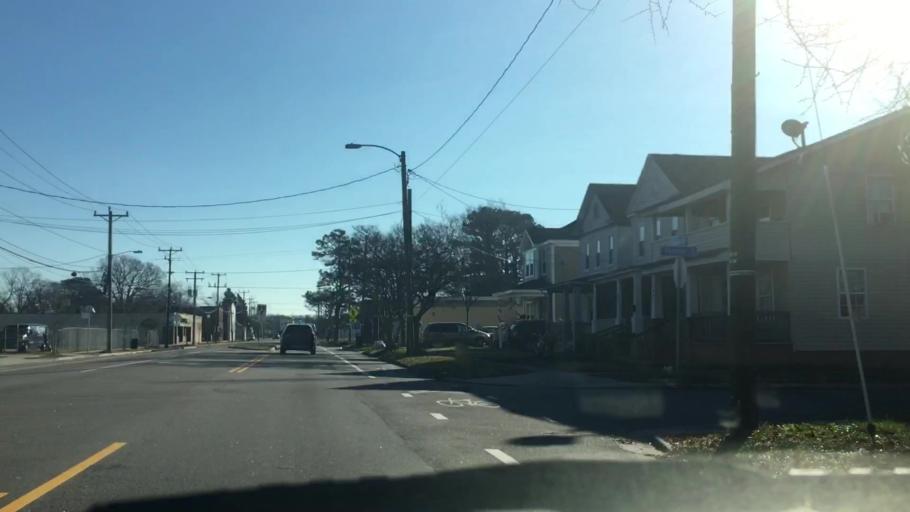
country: US
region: Virginia
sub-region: City of Norfolk
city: Norfolk
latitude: 36.8766
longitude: -76.2595
